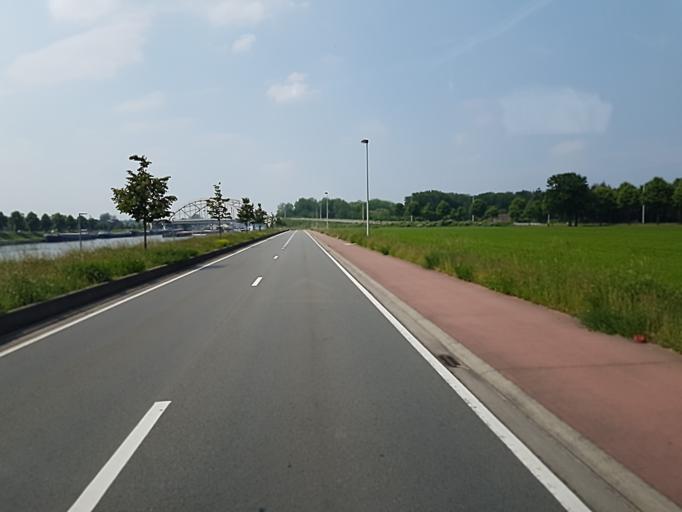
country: BE
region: Flanders
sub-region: Provincie Antwerpen
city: Wijnegem
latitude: 51.2327
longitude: 4.5230
